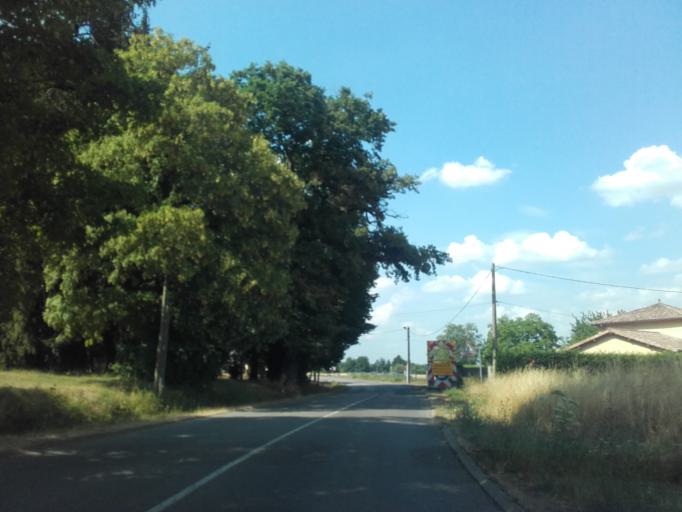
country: FR
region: Bourgogne
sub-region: Departement de Saone-et-Loire
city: Creches-sur-Saone
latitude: 46.2541
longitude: 4.7818
